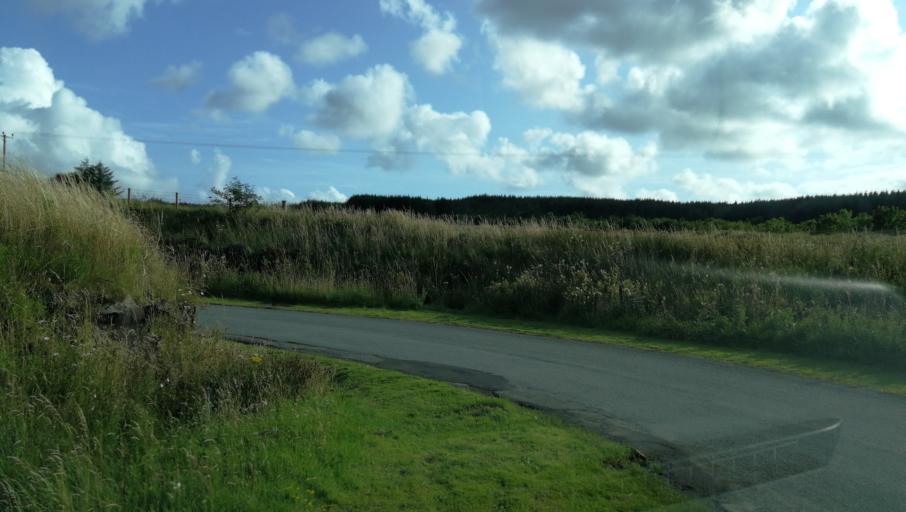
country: GB
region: Scotland
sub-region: Highland
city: Isle of Skye
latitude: 57.4713
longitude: -6.4382
